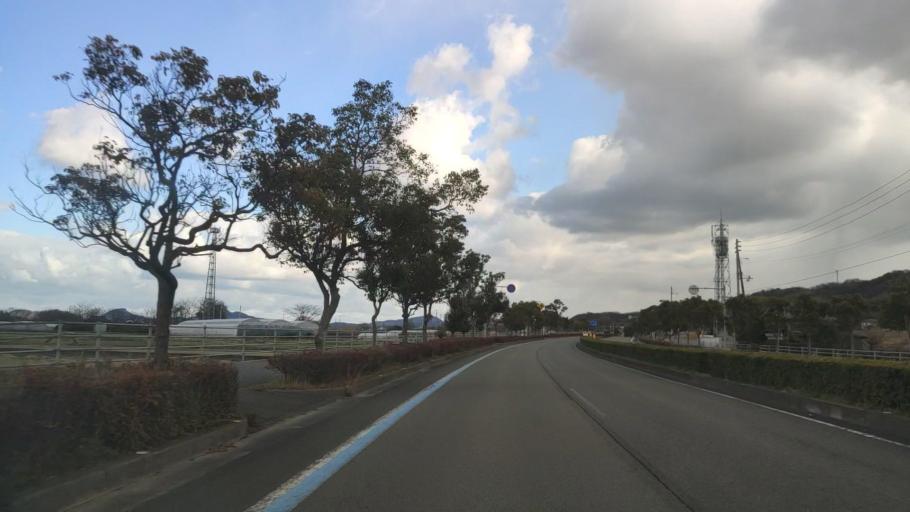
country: JP
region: Ehime
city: Hojo
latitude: 33.9336
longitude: 132.7676
